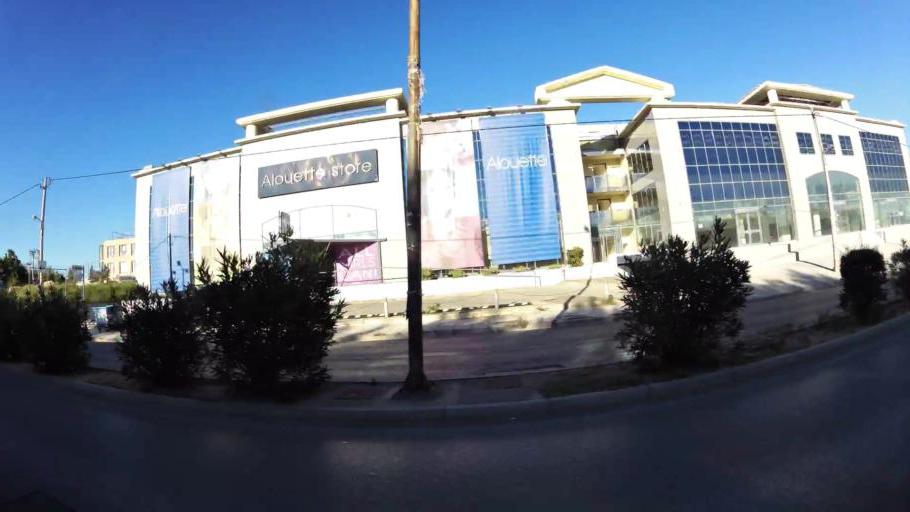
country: GR
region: Attica
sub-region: Nomarchia Athinas
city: Melissia
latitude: 38.0459
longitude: 23.8404
